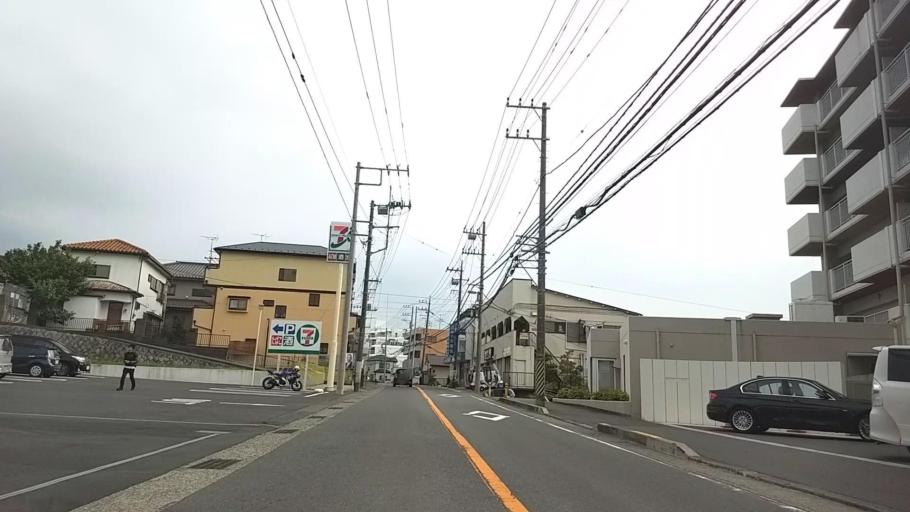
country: JP
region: Kanagawa
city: Minami-rinkan
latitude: 35.4659
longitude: 139.4216
